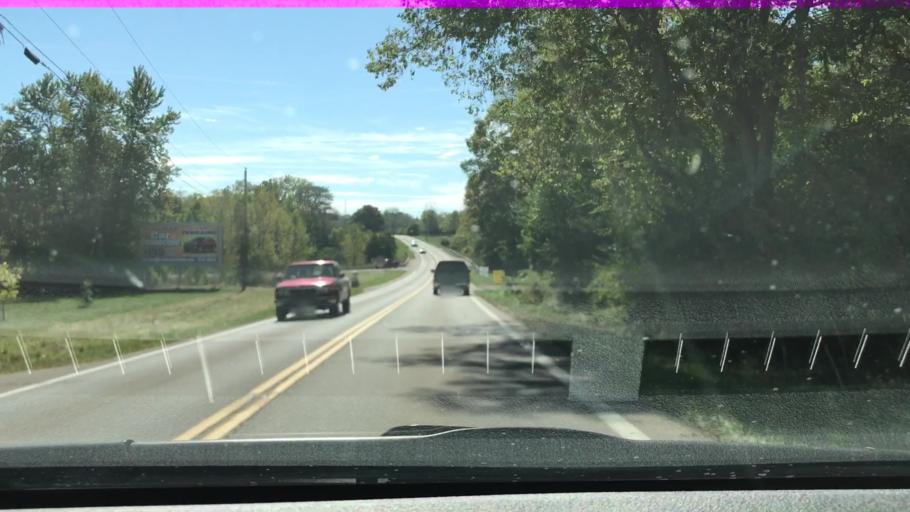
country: US
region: Ohio
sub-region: Butler County
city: Hamilton
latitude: 39.4620
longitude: -84.6281
